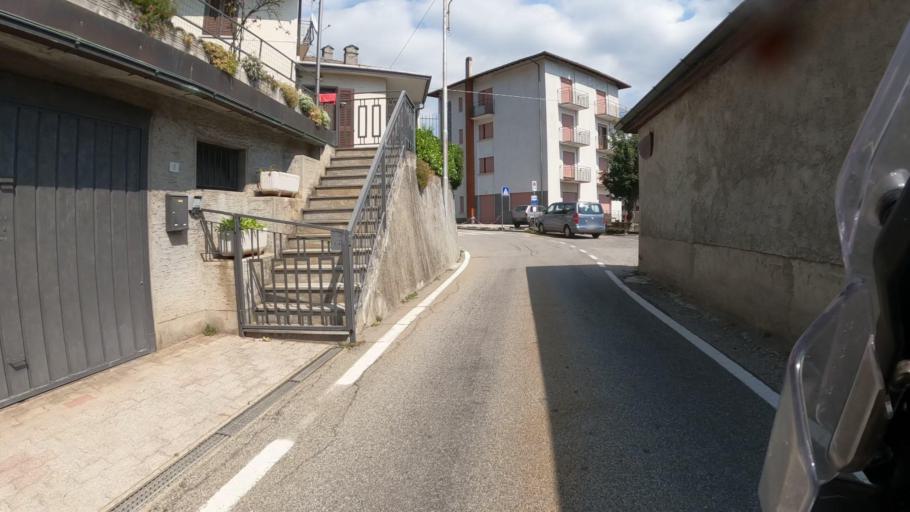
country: IT
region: Lombardy
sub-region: Provincia di Varese
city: Veddasca
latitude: 46.0707
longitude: 8.7977
